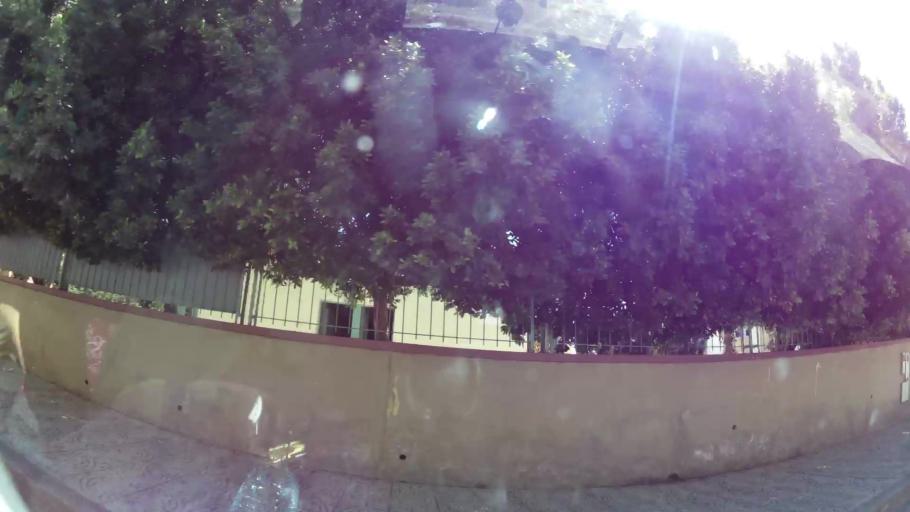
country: MA
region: Meknes-Tafilalet
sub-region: Meknes
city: Meknes
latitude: 33.8897
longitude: -5.5740
